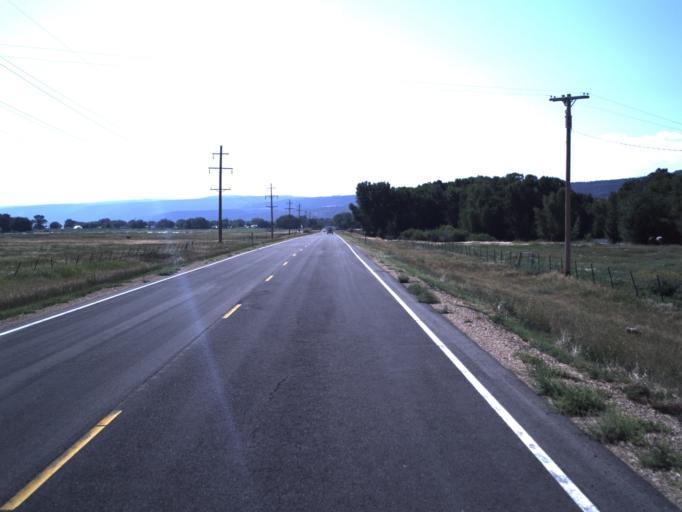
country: US
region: Utah
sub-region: Duchesne County
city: Duchesne
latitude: 40.3660
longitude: -110.7227
